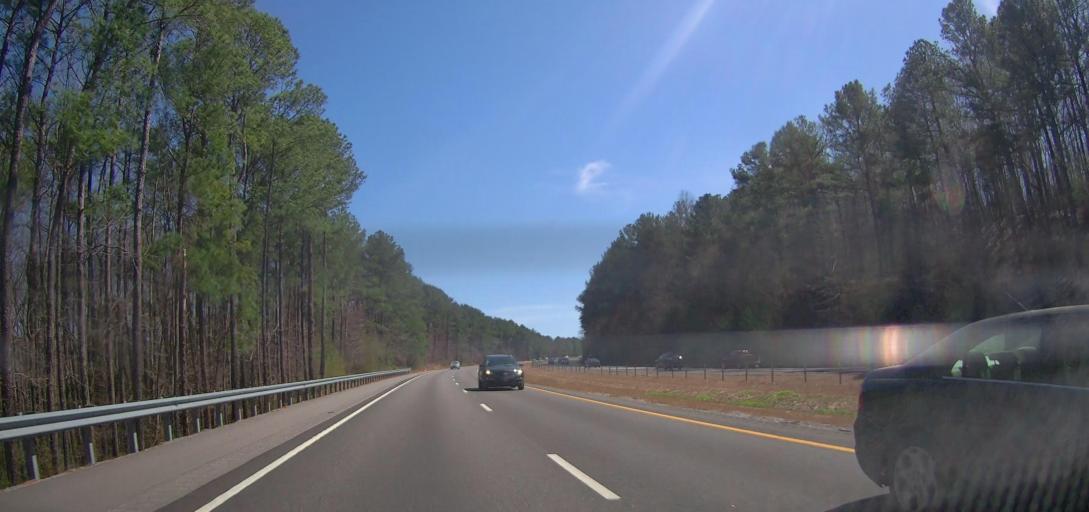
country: US
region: Alabama
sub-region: Morgan County
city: Falkville
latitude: 34.2820
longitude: -86.9025
